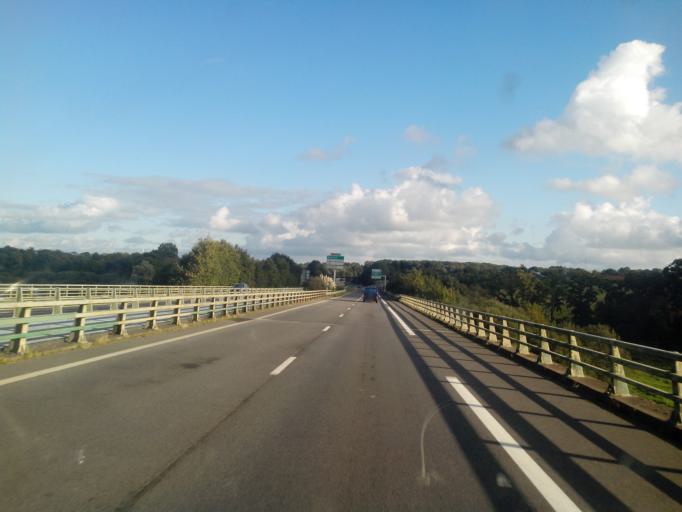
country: FR
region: Pays de la Loire
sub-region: Departement de la Loire-Atlantique
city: Pontchateau
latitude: 47.4416
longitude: -2.0792
